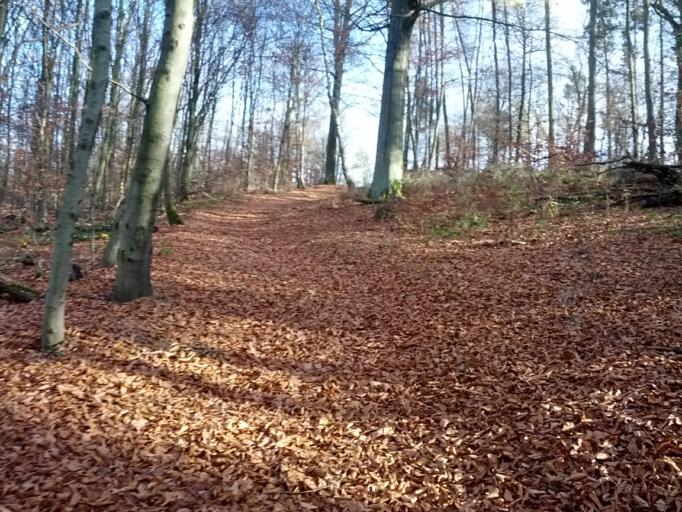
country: DE
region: Thuringia
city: Wolfsburg-Unkeroda
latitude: 50.9460
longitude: 10.2898
